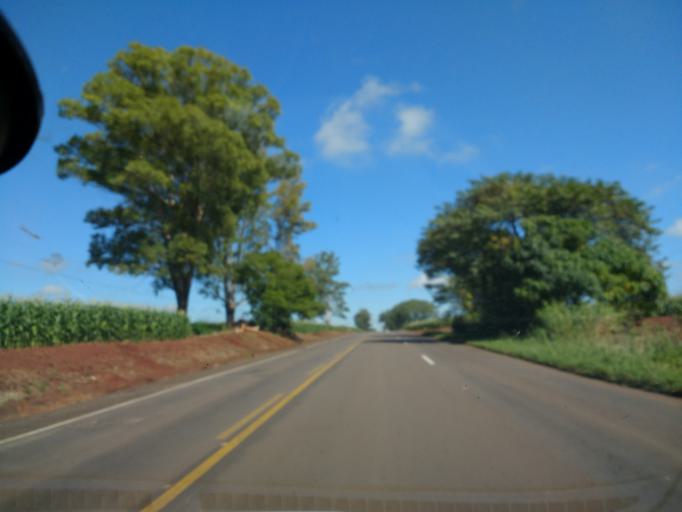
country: BR
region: Parana
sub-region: Terra Boa
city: Terra Boa
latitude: -23.6005
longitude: -52.3997
